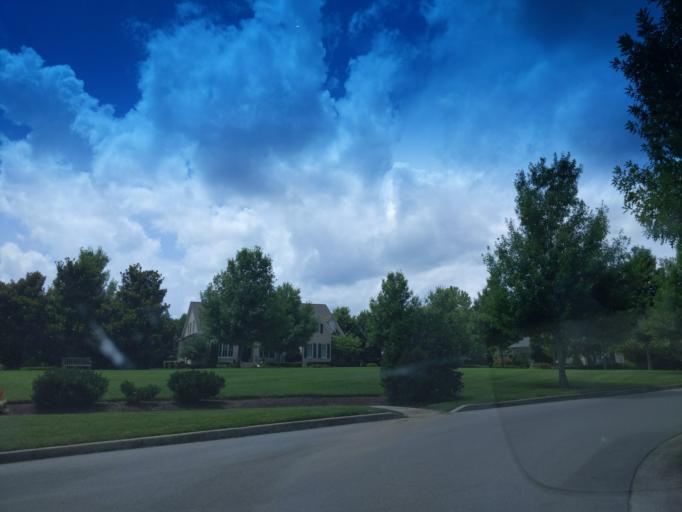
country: US
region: Tennessee
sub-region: Williamson County
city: Brentwood Estates
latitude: 36.0220
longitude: -86.7739
